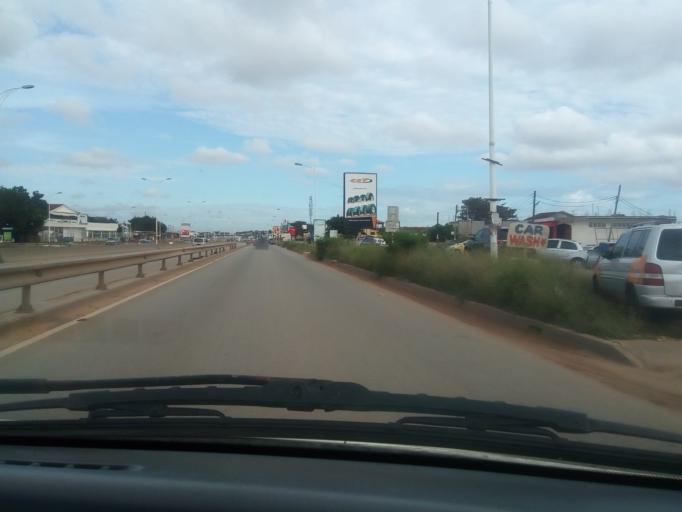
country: GH
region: Greater Accra
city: Dome
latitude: 5.6566
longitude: -0.2639
